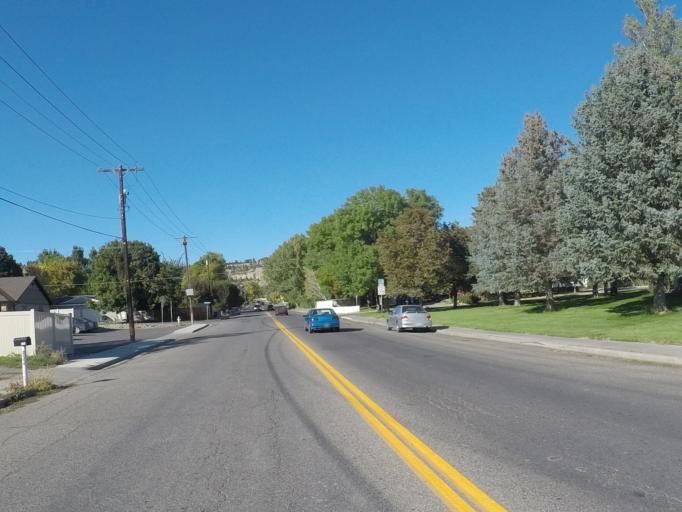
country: US
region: Montana
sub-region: Yellowstone County
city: Billings
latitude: 45.7916
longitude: -108.5904
